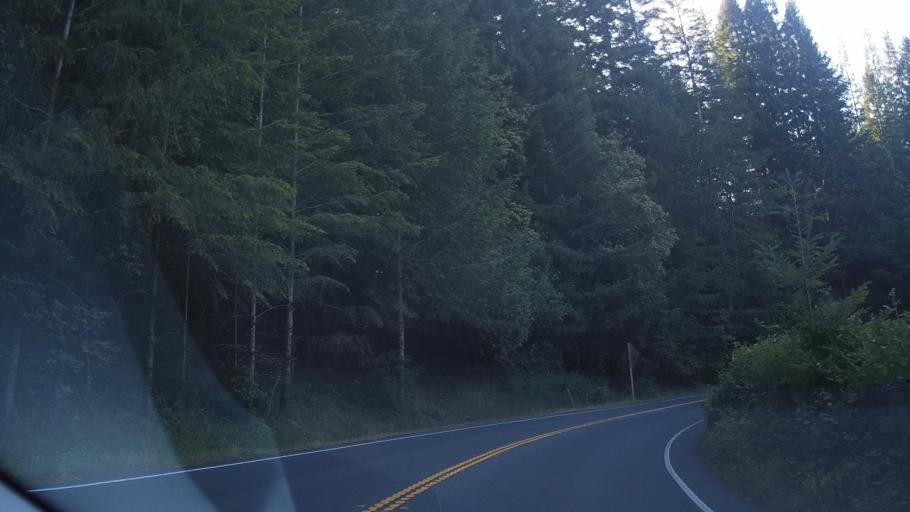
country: US
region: California
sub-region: Mendocino County
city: Fort Bragg
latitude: 39.3574
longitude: -123.6183
